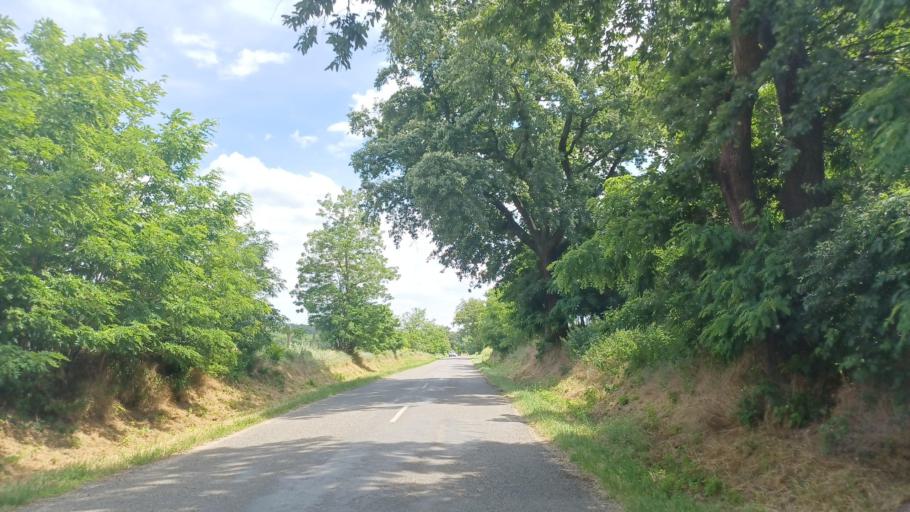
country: HU
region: Tolna
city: Simontornya
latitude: 46.7027
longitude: 18.5139
